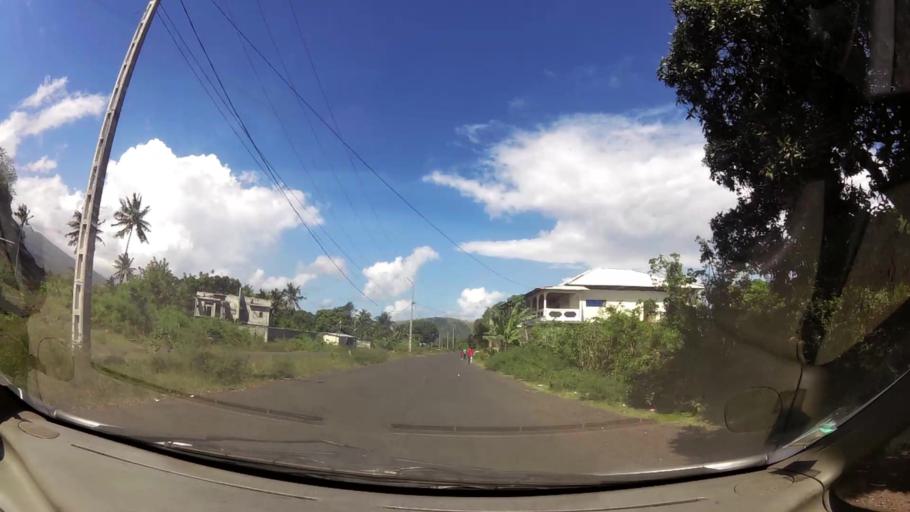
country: KM
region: Grande Comore
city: Mavingouni
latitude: -11.7357
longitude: 43.2403
